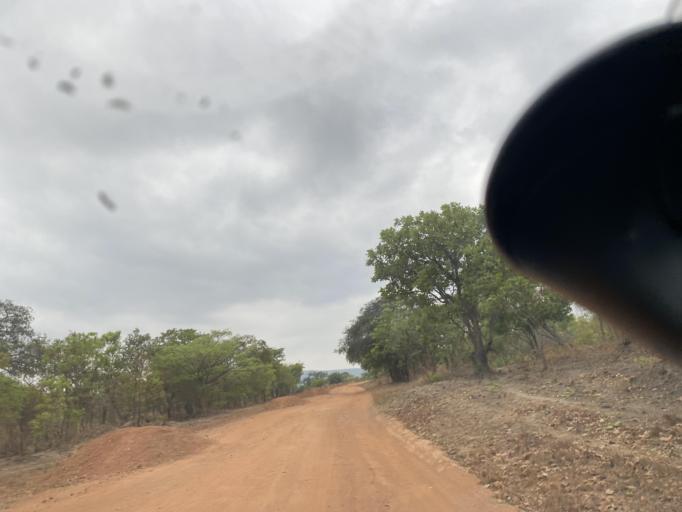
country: ZM
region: Lusaka
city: Chongwe
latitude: -15.2166
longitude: 28.7538
